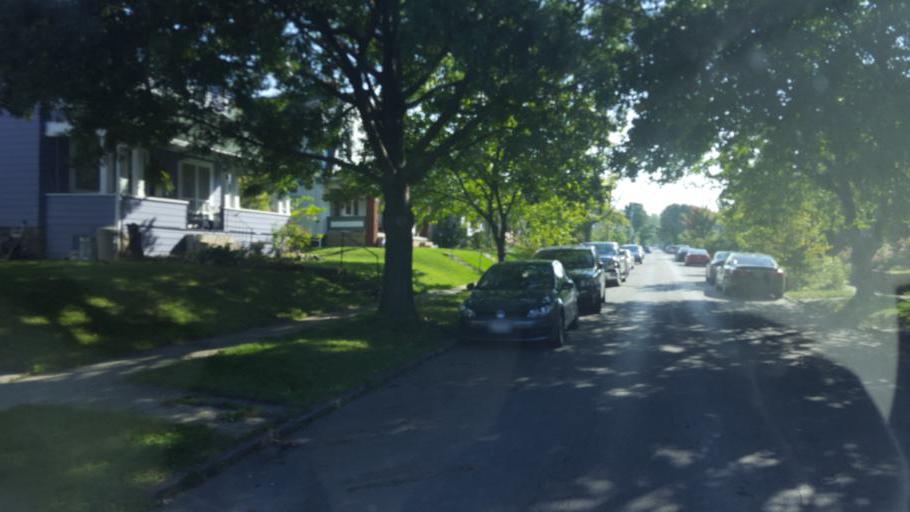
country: US
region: Ohio
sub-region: Franklin County
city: Grandview Heights
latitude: 40.0216
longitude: -83.0109
